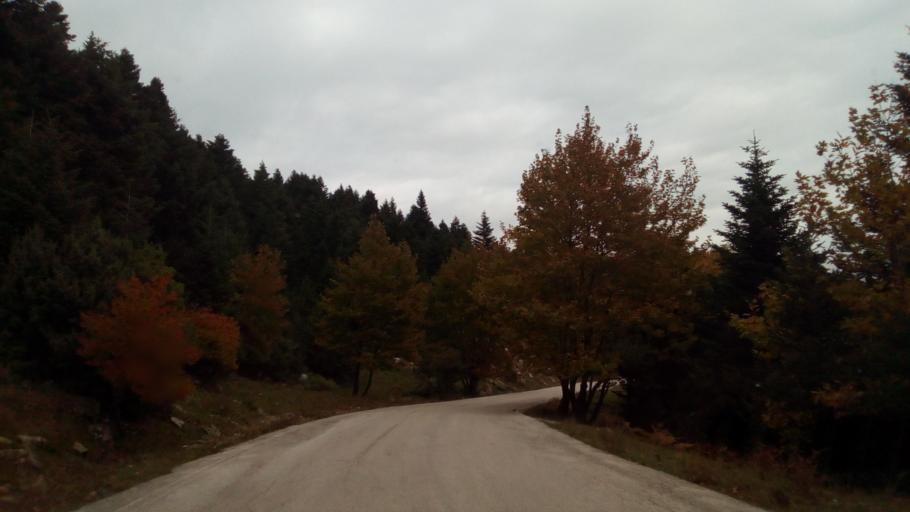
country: GR
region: West Greece
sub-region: Nomos Aitolias kai Akarnanias
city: Thermo
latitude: 38.6222
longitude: 21.8211
